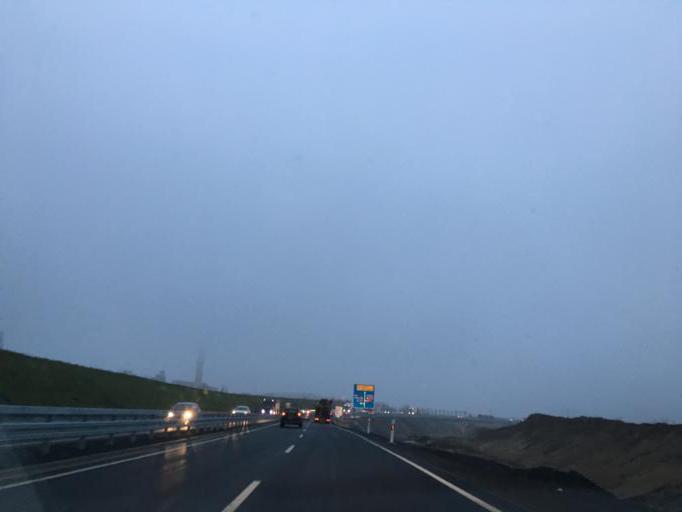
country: DE
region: Saxony
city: Borna
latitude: 51.1388
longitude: 12.5074
